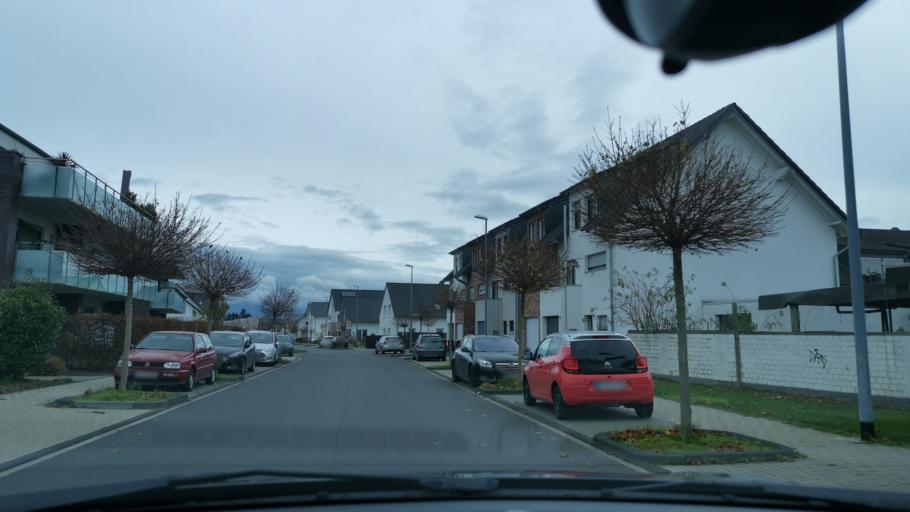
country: DE
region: North Rhine-Westphalia
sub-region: Regierungsbezirk Dusseldorf
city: Rommerskirchen
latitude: 51.0382
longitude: 6.6829
